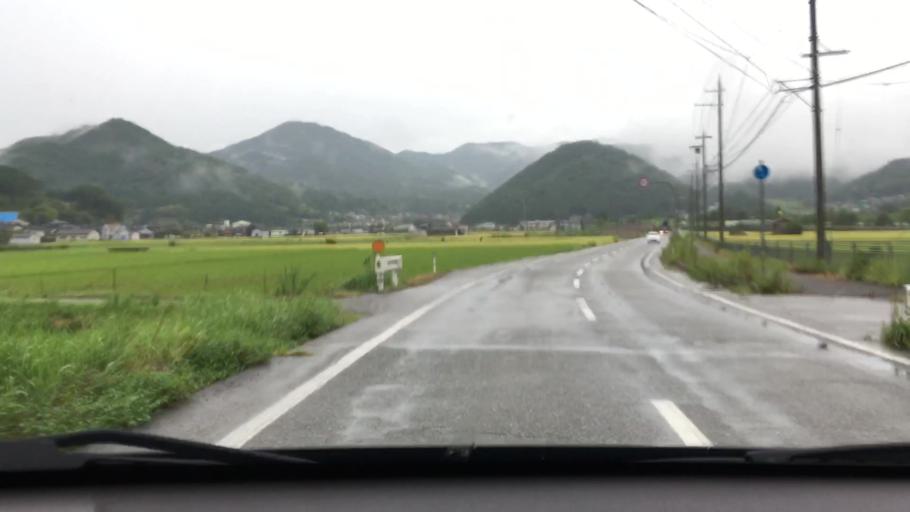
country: JP
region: Hyogo
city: Toyooka
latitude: 35.3118
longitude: 134.8507
